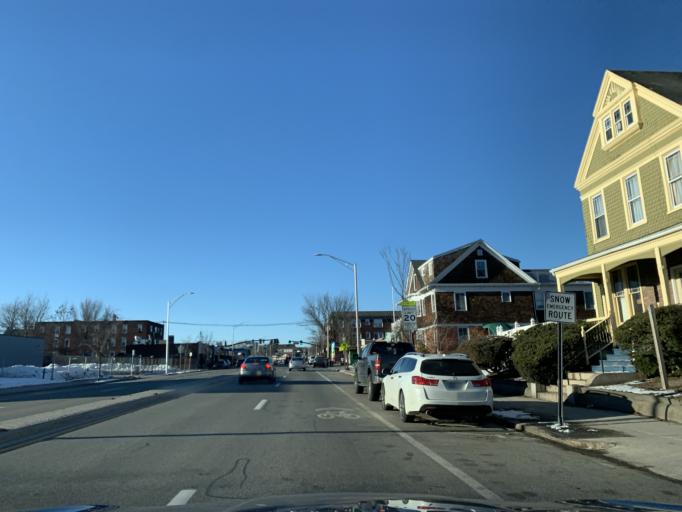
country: US
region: Rhode Island
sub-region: Providence County
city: Cranston
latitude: 41.7946
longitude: -71.4243
